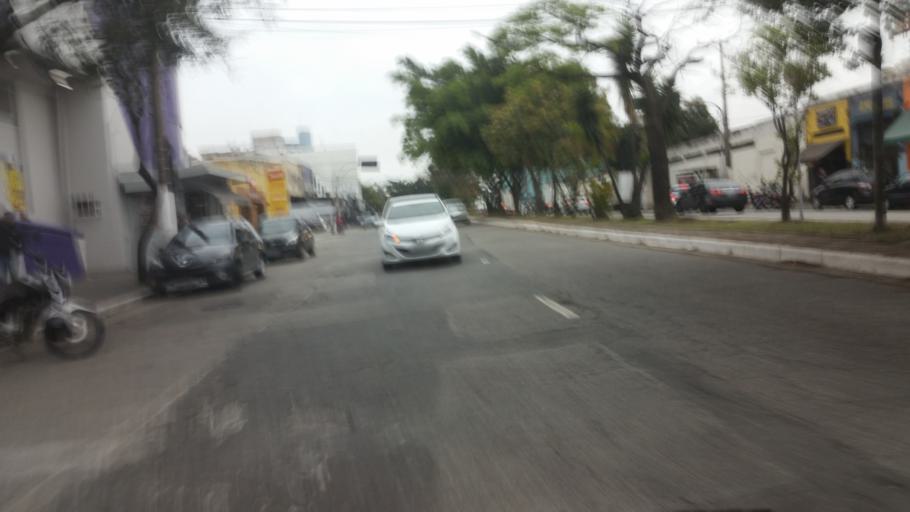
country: BR
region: Sao Paulo
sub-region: Diadema
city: Diadema
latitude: -23.6242
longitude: -46.6199
